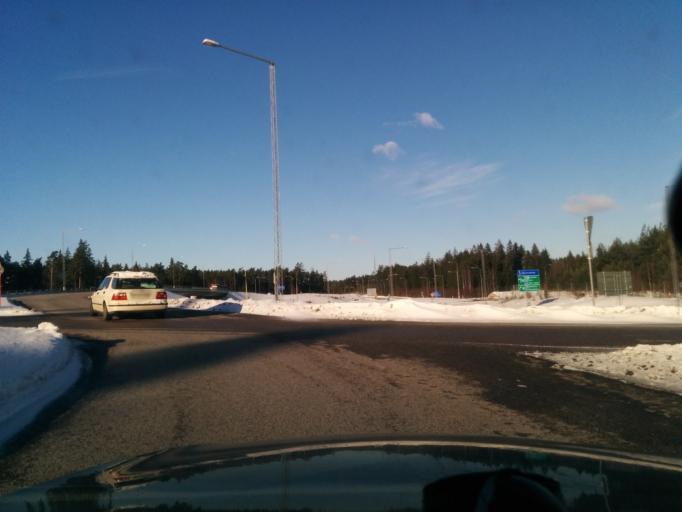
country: SE
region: Stockholm
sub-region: Vallentuna Kommun
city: Vallentuna
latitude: 59.4874
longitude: 18.1114
